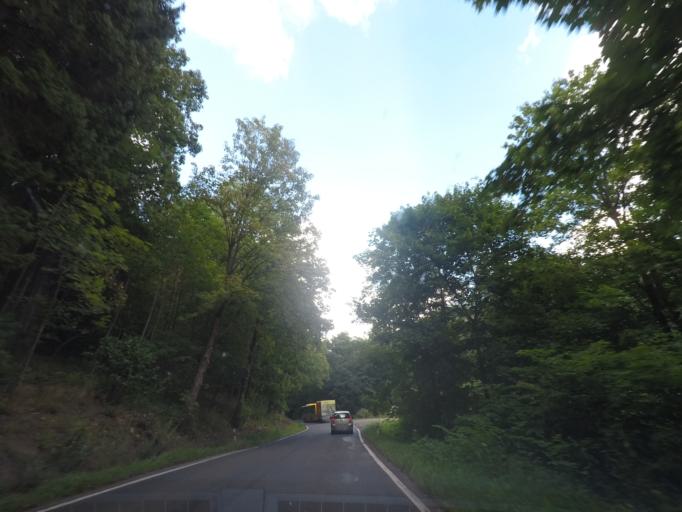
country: CZ
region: Kralovehradecky
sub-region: Okres Trutnov
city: Trutnov
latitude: 50.5840
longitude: 15.9727
